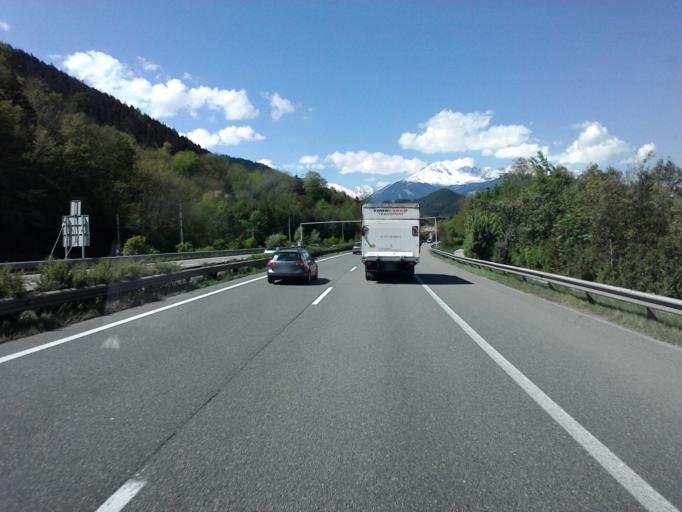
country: AT
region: Tyrol
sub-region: Politischer Bezirk Innsbruck Land
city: Vols
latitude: 47.2532
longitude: 11.3463
